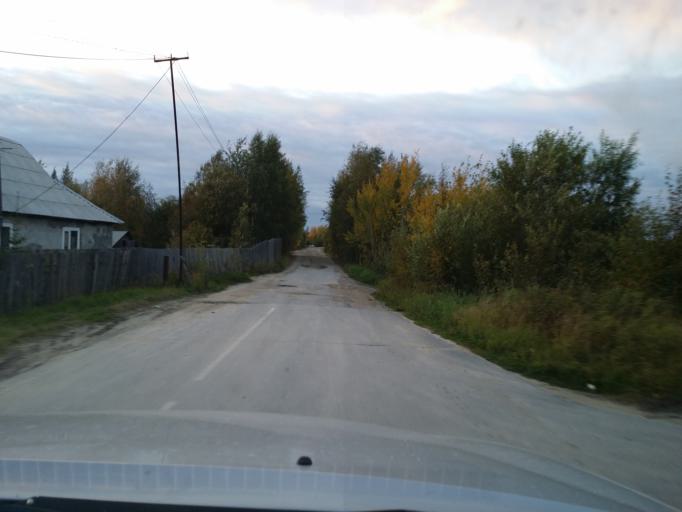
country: RU
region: Khanty-Mansiyskiy Avtonomnyy Okrug
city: Megion
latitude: 61.0799
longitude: 76.1550
